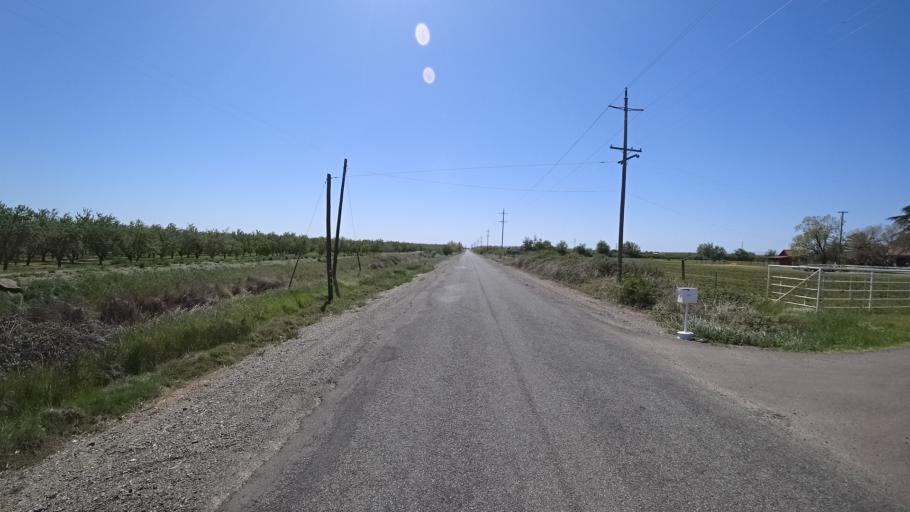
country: US
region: California
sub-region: Glenn County
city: Orland
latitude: 39.7939
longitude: -122.1410
